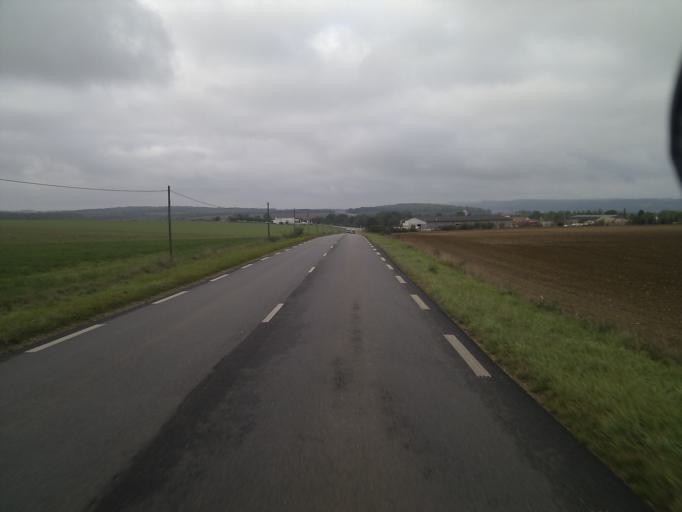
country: FR
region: Lorraine
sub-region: Departement des Vosges
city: Neufchateau
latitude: 48.4141
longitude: 5.7502
